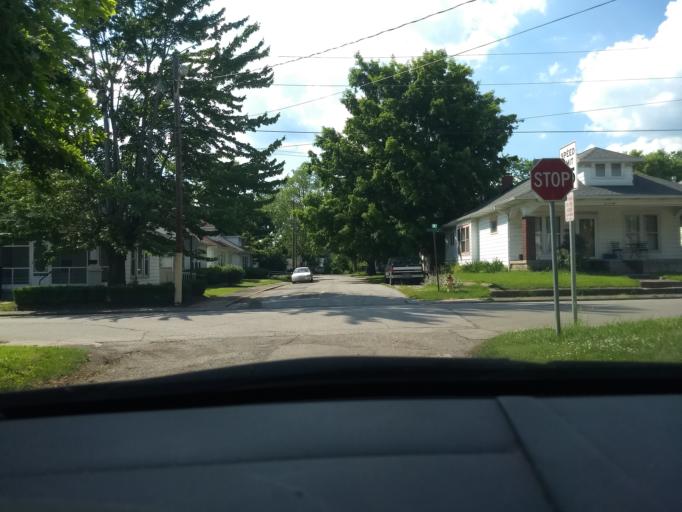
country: US
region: Indiana
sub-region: Floyd County
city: New Albany
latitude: 38.2974
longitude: -85.8305
